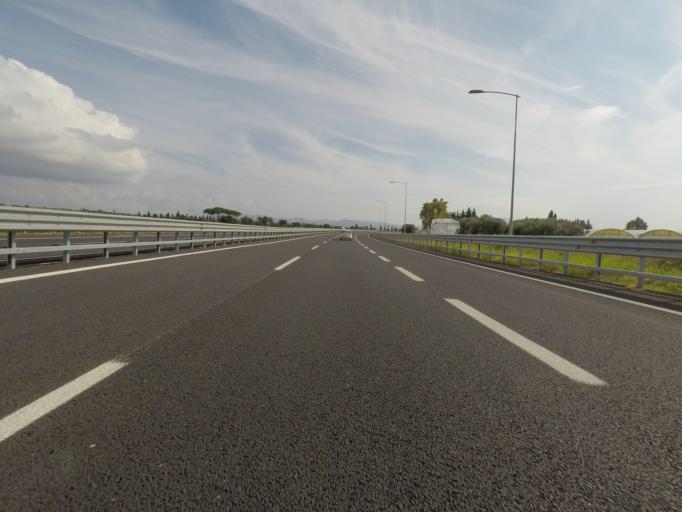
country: IT
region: Latium
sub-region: Provincia di Viterbo
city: Tarquinia
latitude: 42.2342
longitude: 11.7633
